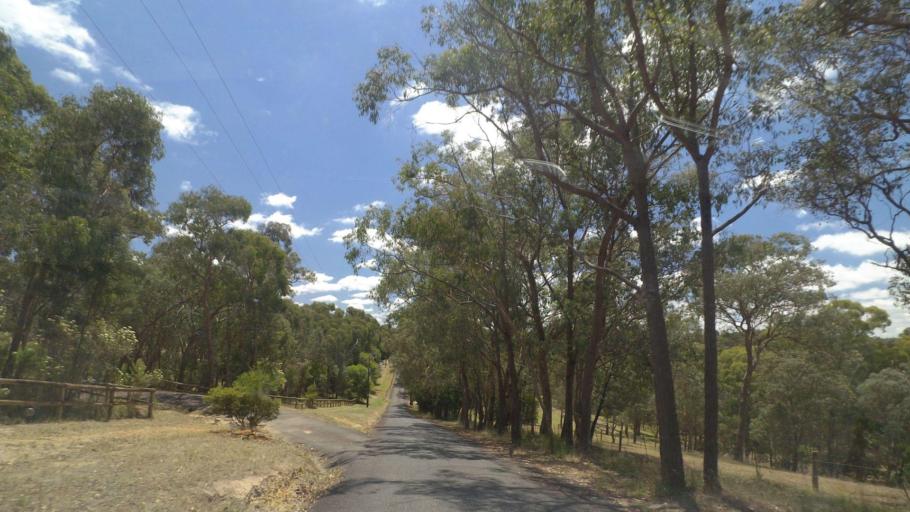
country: AU
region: Victoria
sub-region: Manningham
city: Warrandyte
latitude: -37.7281
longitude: 145.2656
